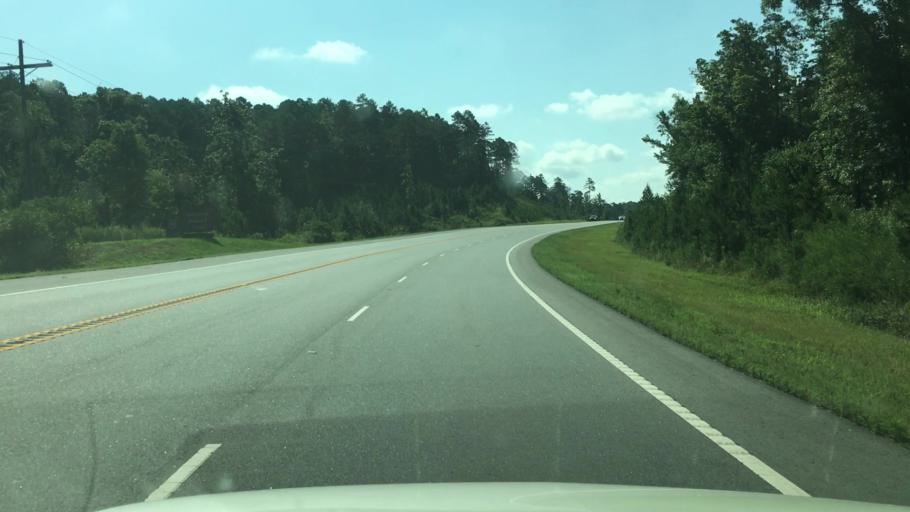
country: US
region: Arkansas
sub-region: Garland County
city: Piney
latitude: 34.5222
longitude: -93.3184
